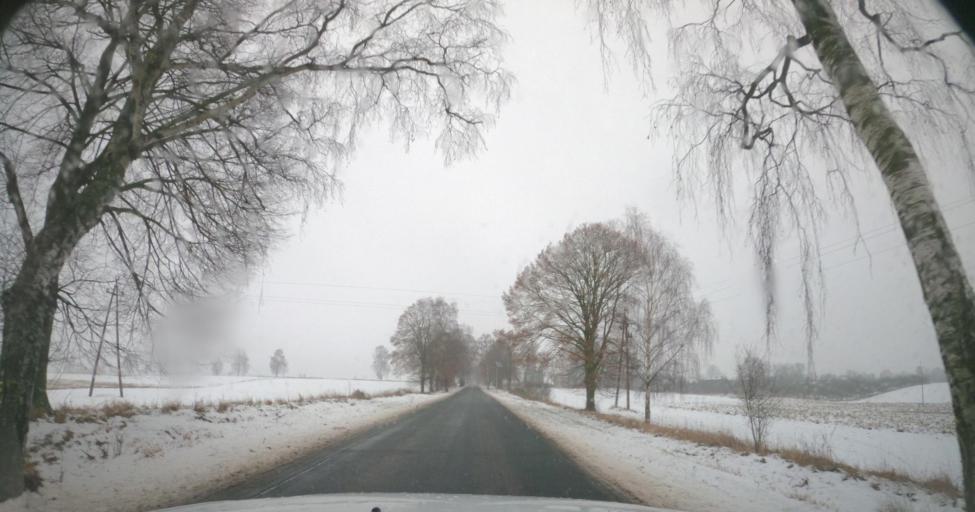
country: PL
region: West Pomeranian Voivodeship
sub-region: Powiat gryficki
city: Gryfice
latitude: 53.9050
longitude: 15.2813
